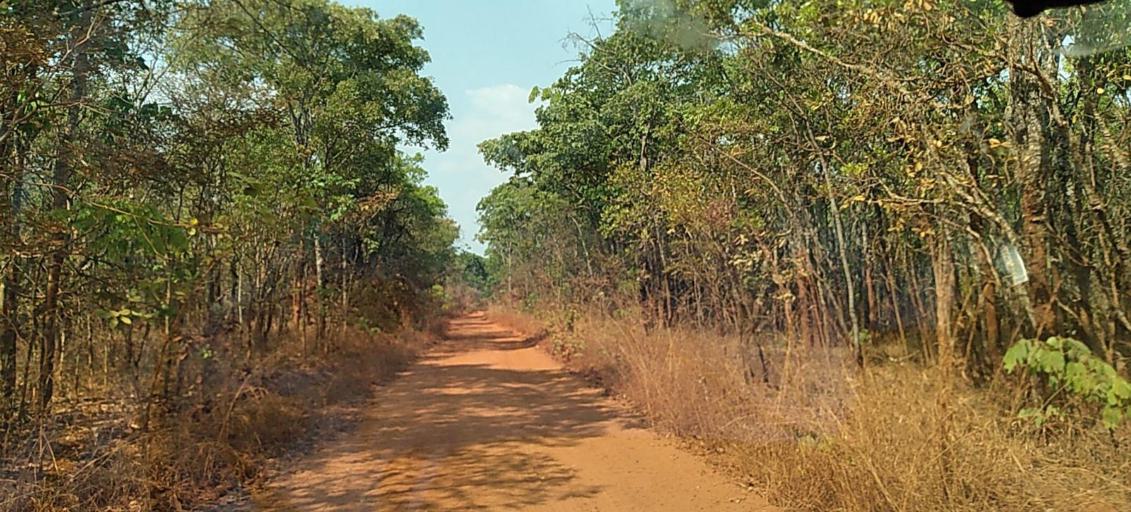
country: ZM
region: North-Western
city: Kasempa
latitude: -13.3177
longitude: 26.0546
